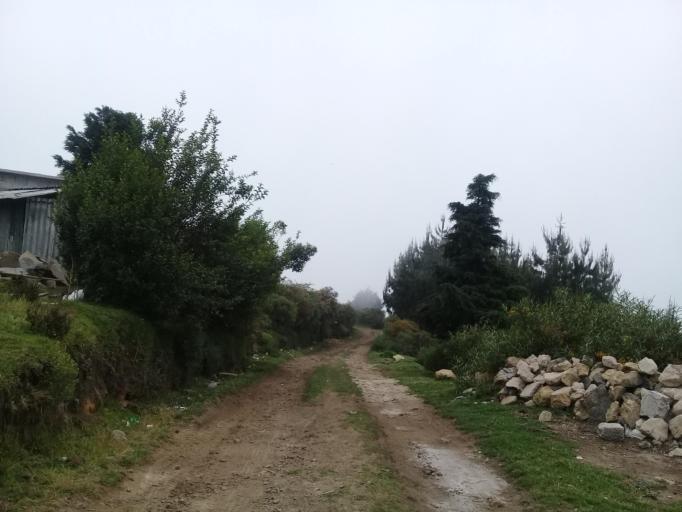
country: MX
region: Veracruz
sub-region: Mariano Escobedo
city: Texmola
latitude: 18.9584
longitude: -97.2172
